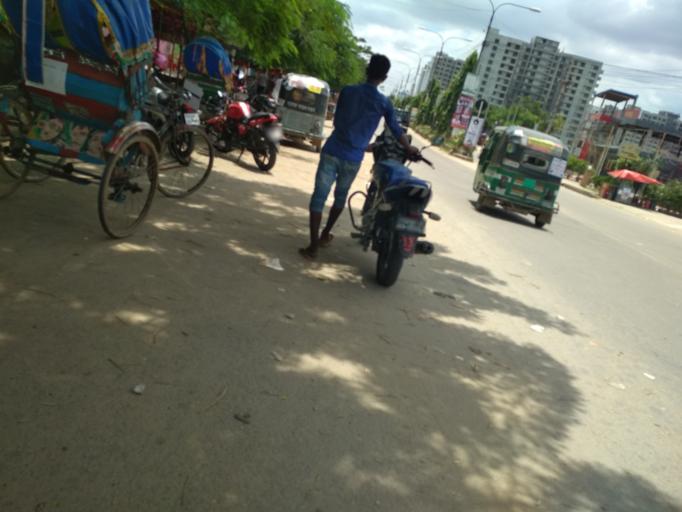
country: BD
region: Dhaka
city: Tungi
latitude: 23.8362
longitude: 90.3765
